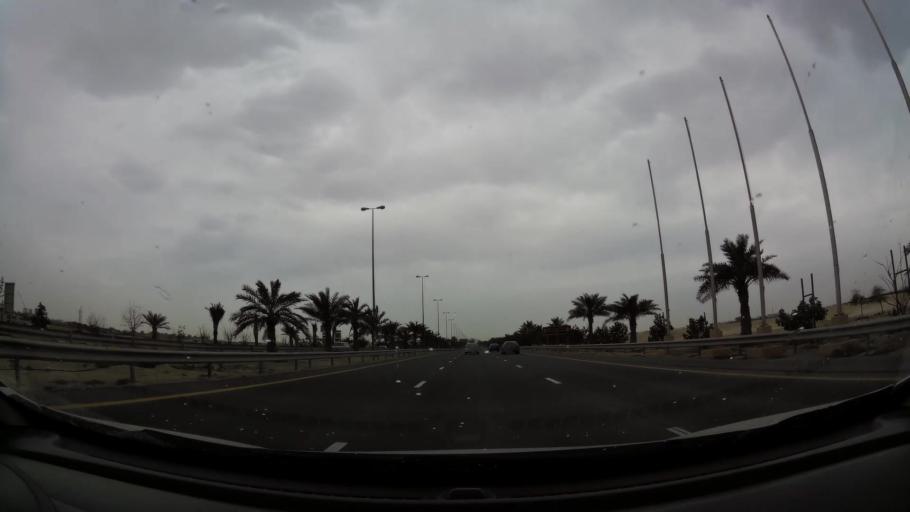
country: BH
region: Central Governorate
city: Dar Kulayb
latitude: 26.0863
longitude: 50.5395
